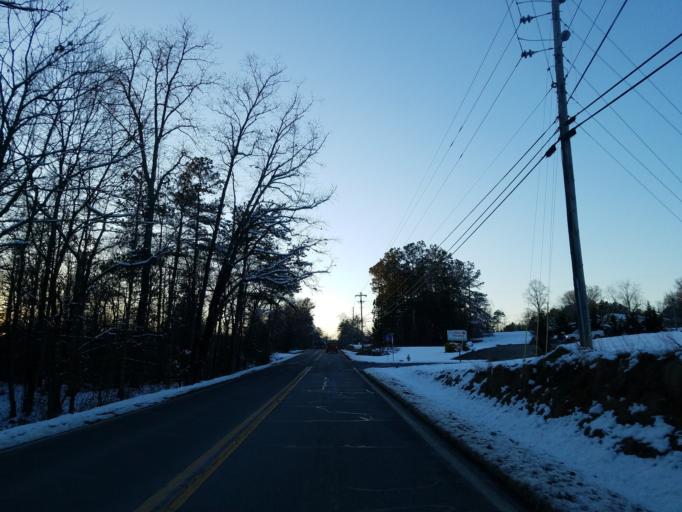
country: US
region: Georgia
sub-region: Pickens County
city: Nelson
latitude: 34.4124
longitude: -84.2882
